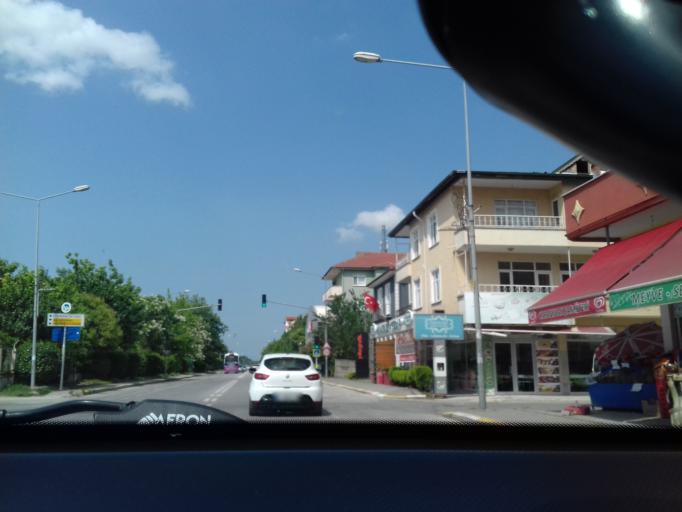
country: TR
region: Sakarya
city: Adapazari
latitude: 40.7202
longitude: 30.3684
